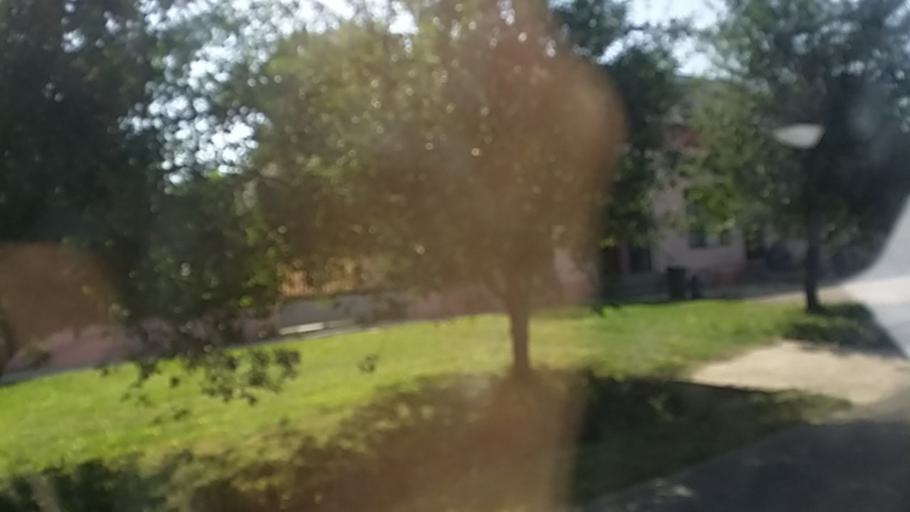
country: HU
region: Baranya
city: Siklos
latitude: 45.9142
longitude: 18.3363
